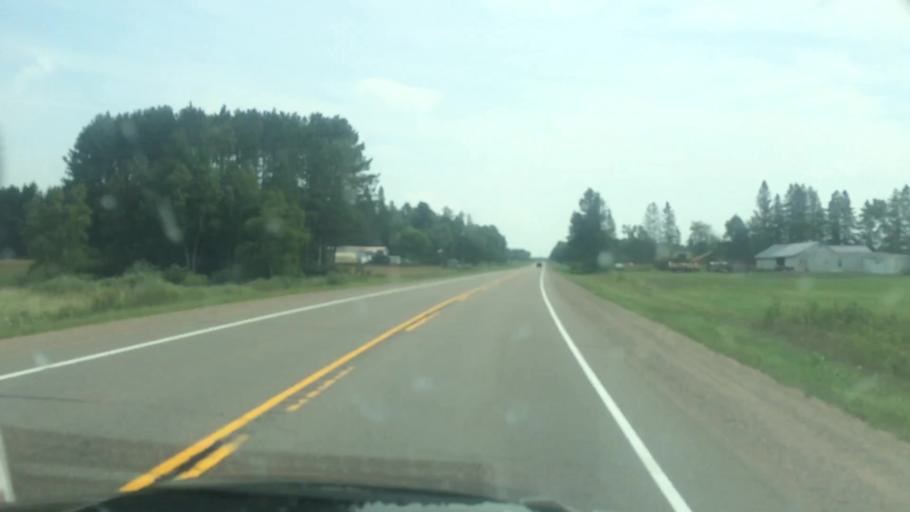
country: US
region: Wisconsin
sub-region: Langlade County
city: Antigo
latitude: 45.1469
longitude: -89.2782
